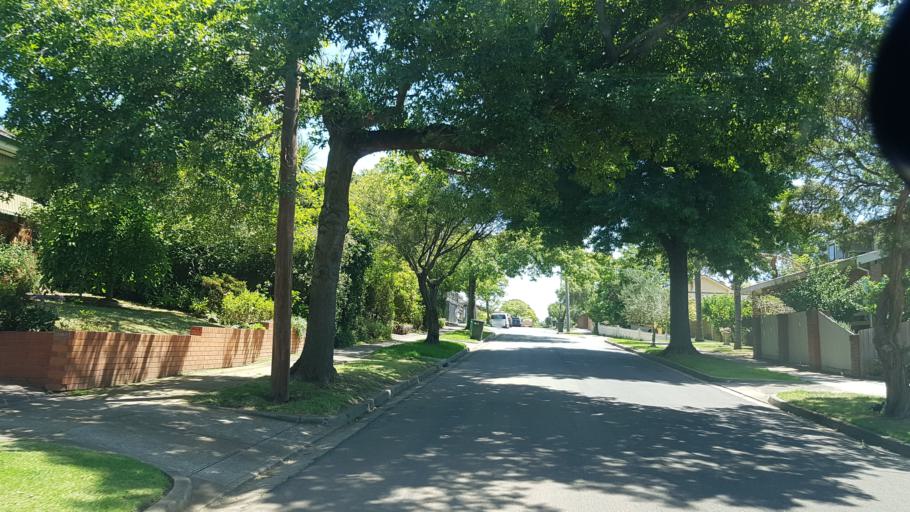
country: AU
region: Victoria
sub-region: Banyule
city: Darch
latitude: -37.7580
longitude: 145.1005
